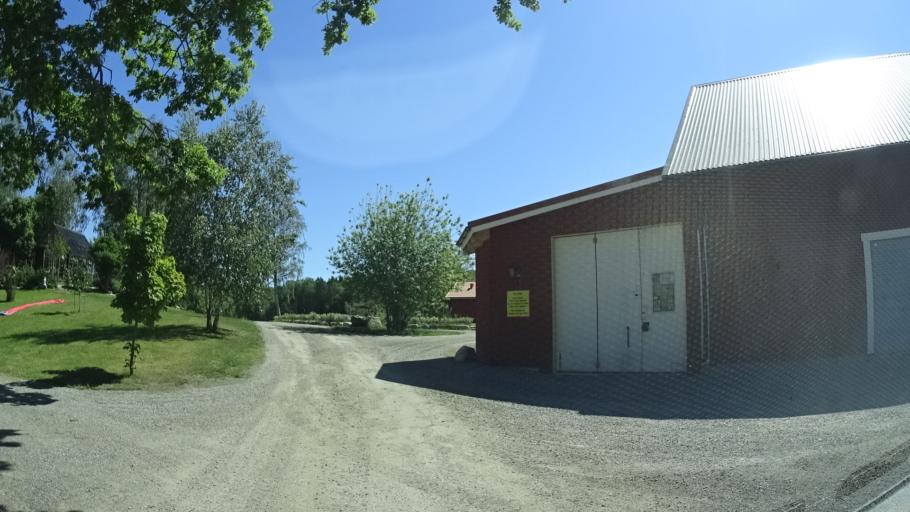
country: SE
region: Stockholm
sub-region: Vallentuna Kommun
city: Vallentuna
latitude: 59.6129
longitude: 18.1632
